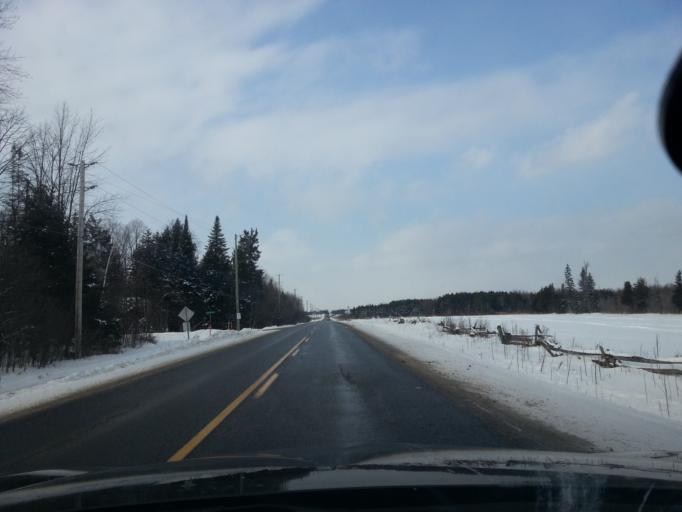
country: CA
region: Ontario
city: Carleton Place
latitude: 45.1612
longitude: -76.0380
